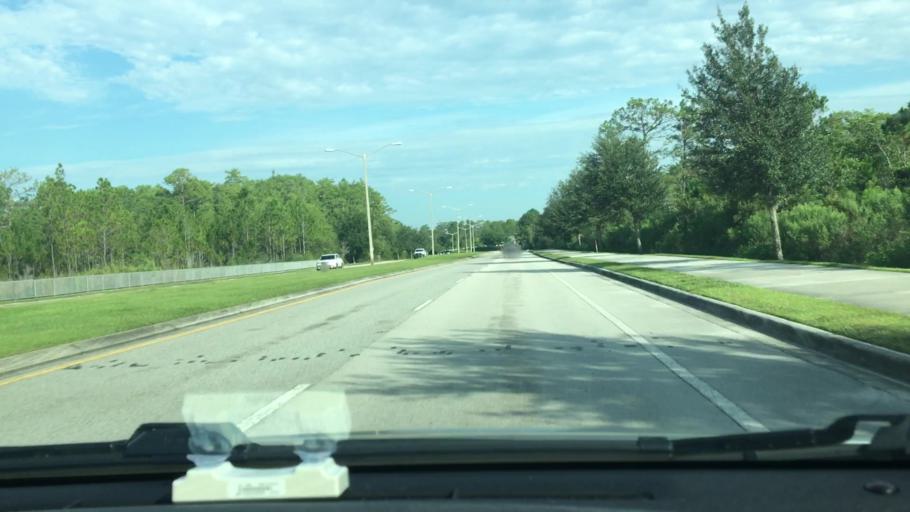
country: US
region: Florida
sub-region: Orange County
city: Conway
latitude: 28.4325
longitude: -81.2426
